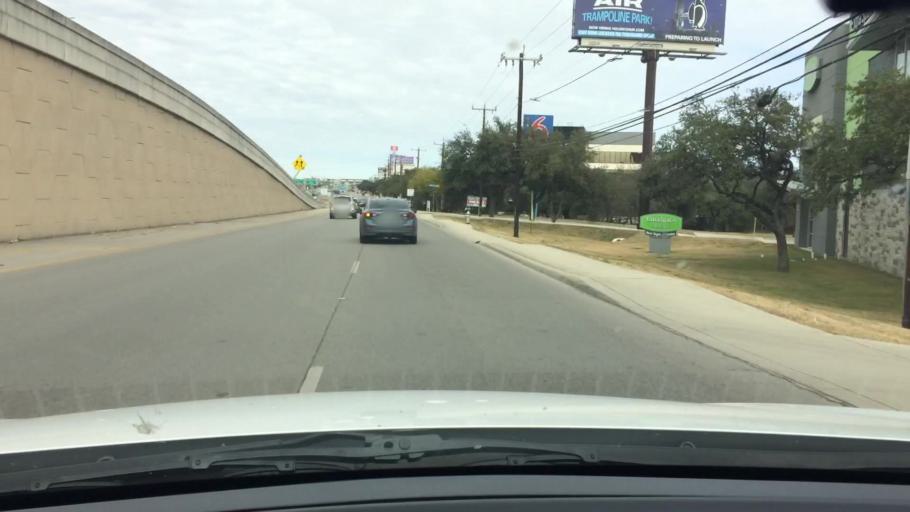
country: US
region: Texas
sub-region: Bexar County
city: Hollywood Park
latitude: 29.5814
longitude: -98.4762
